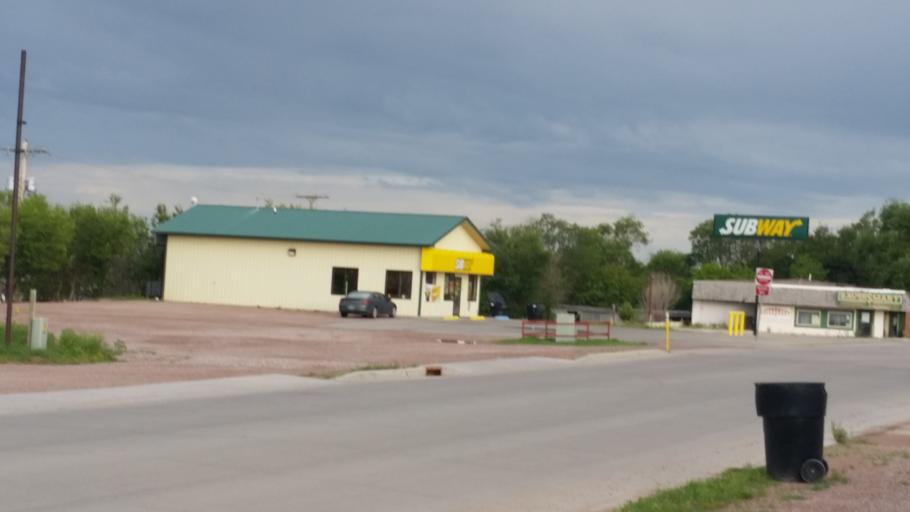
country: US
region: Wyoming
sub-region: Weston County
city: Newcastle
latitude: 43.8482
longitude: -104.1940
